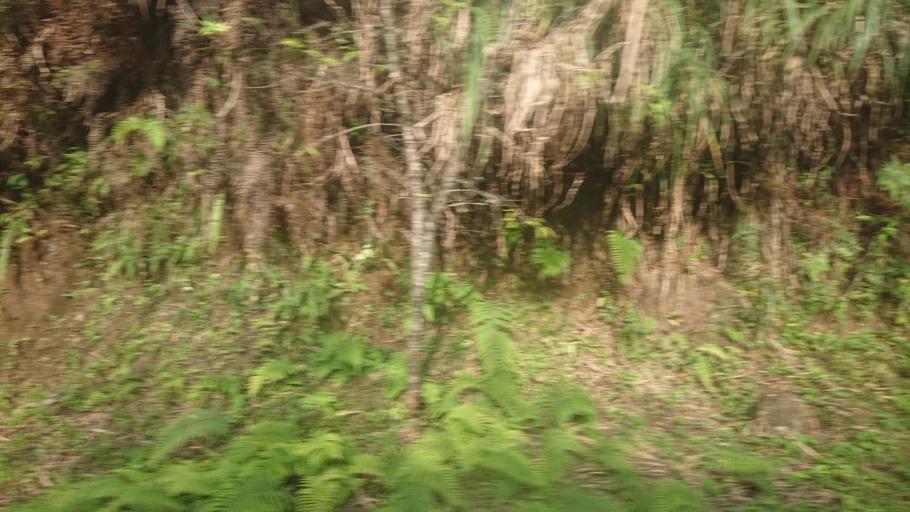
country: TW
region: Taiwan
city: Lugu
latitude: 23.4989
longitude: 120.7891
